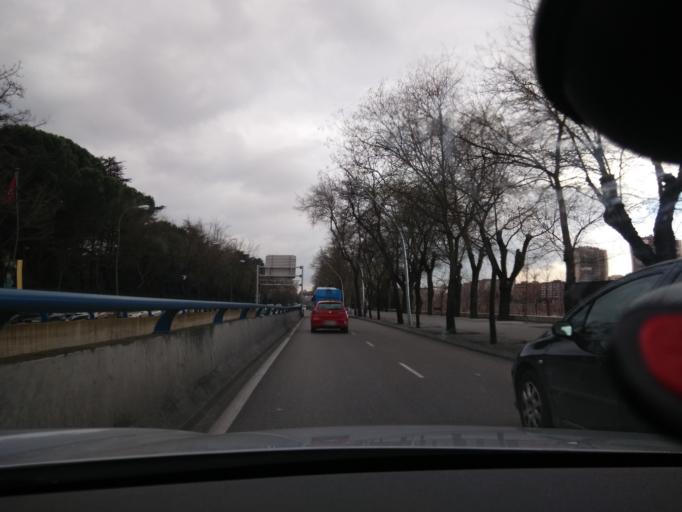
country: ES
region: Madrid
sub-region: Provincia de Madrid
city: City Center
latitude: 40.4189
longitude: -3.7203
